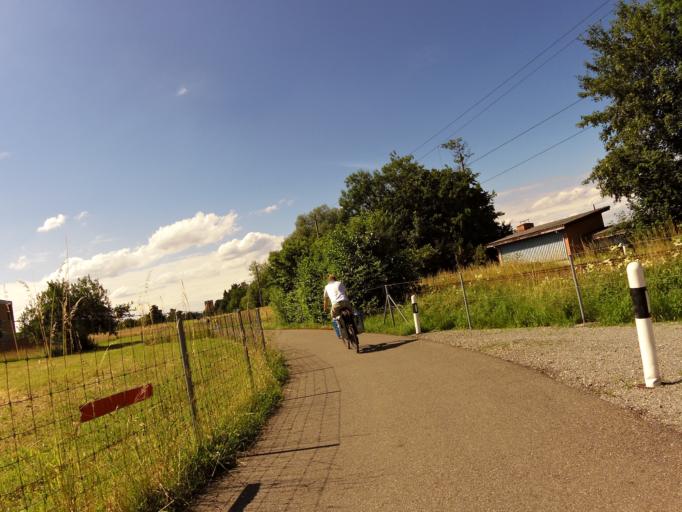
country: CH
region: Thurgau
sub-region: Arbon District
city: Arbon
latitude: 47.5280
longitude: 9.4150
